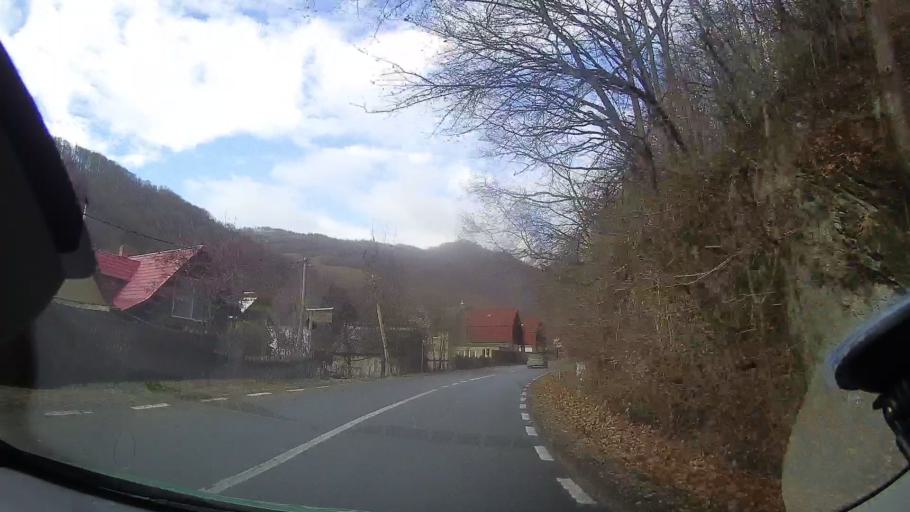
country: RO
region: Cluj
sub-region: Comuna Valea Ierii
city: Valea Ierii
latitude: 46.6146
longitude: 23.4031
